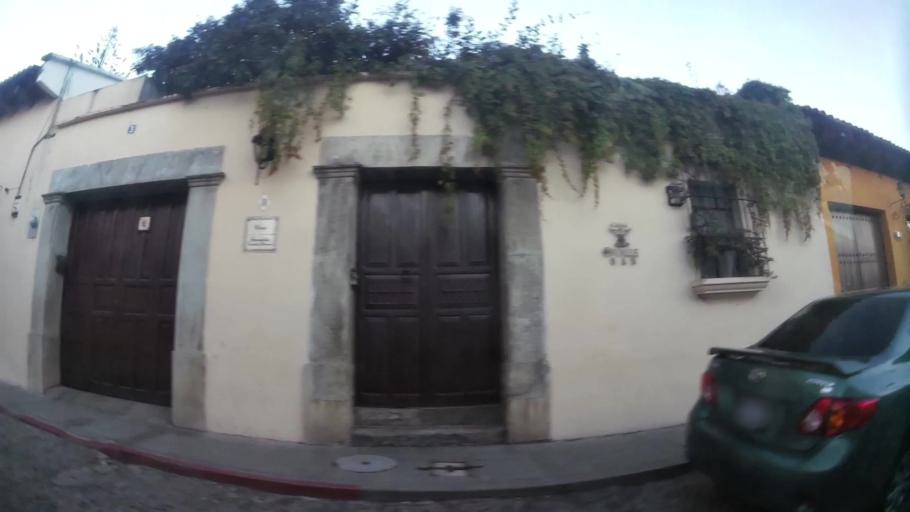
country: GT
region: Sacatepequez
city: Antigua Guatemala
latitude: 14.5568
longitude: -90.7311
